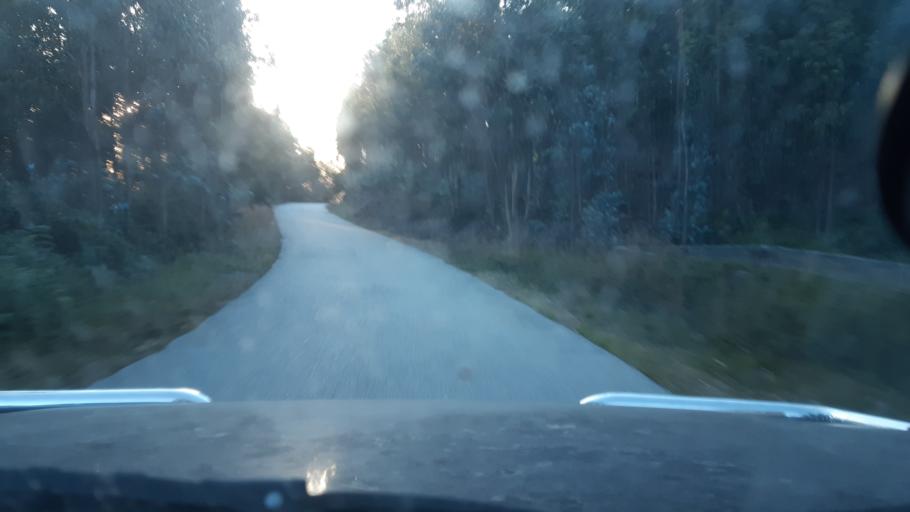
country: PT
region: Aveiro
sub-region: Agueda
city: Aguada de Cima
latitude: 40.5548
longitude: -8.2887
